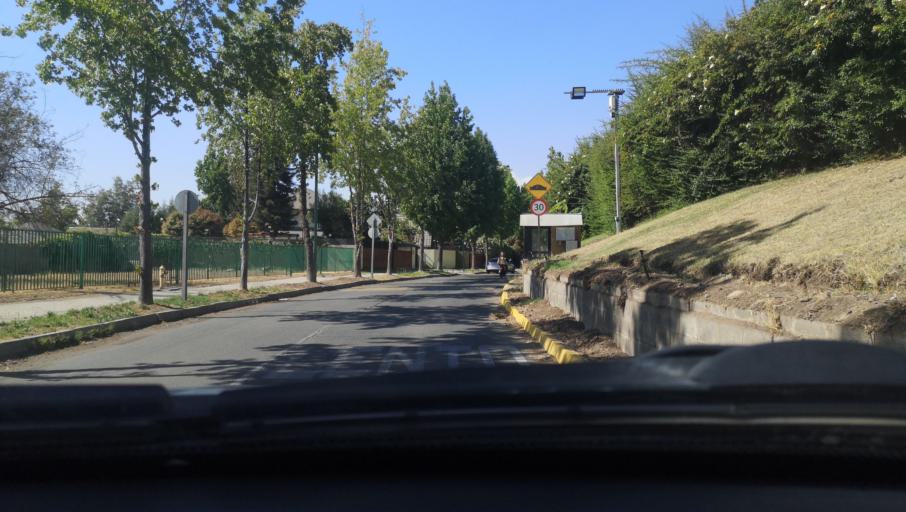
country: CL
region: Santiago Metropolitan
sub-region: Provincia de Santiago
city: Villa Presidente Frei, Nunoa, Santiago, Chile
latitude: -33.4847
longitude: -70.5377
